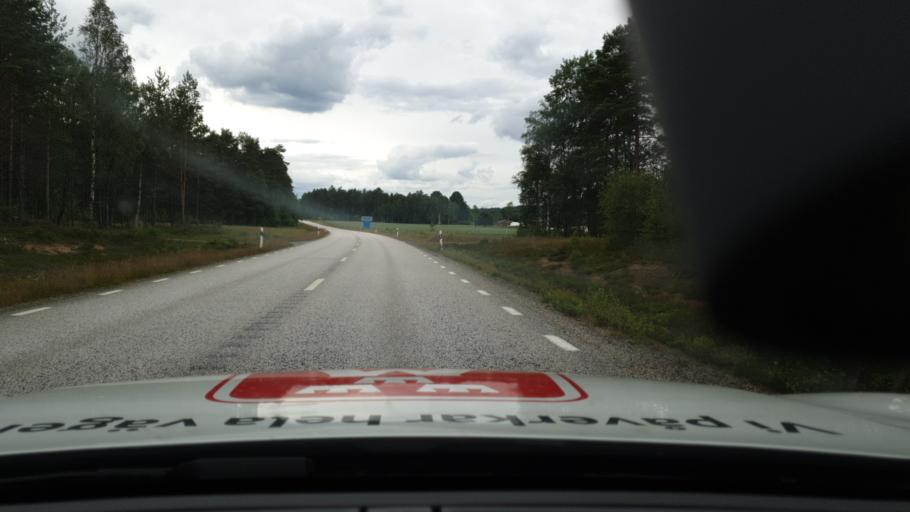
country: SE
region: Joenkoeping
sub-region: Gnosjo Kommun
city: Hillerstorp
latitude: 57.2880
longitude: 13.8307
